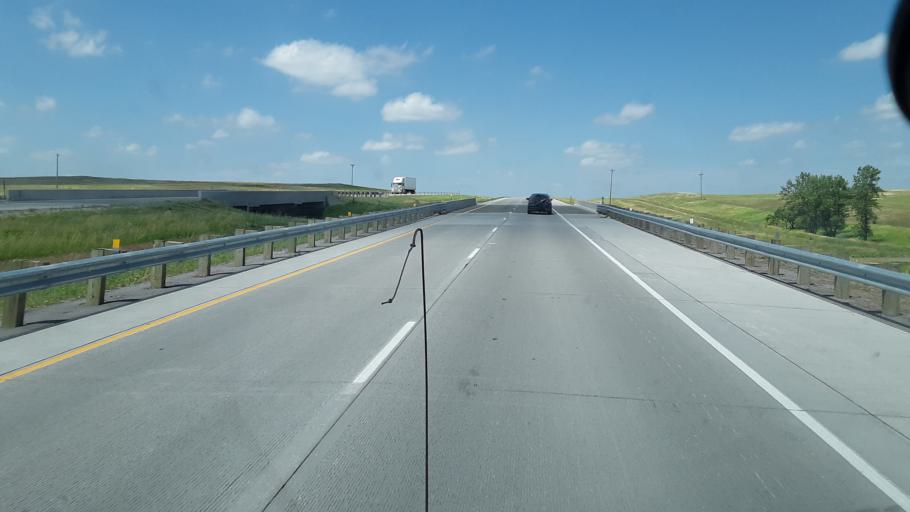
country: US
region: South Dakota
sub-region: Jackson County
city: Kadoka
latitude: 43.8471
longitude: -101.3418
